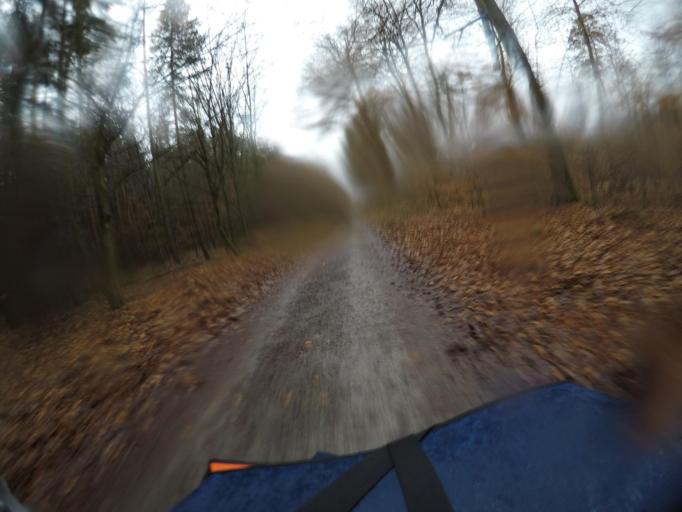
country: DE
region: Baden-Wuerttemberg
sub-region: Karlsruhe Region
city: Linkenheim-Hochstetten
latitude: 49.1168
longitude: 8.4475
